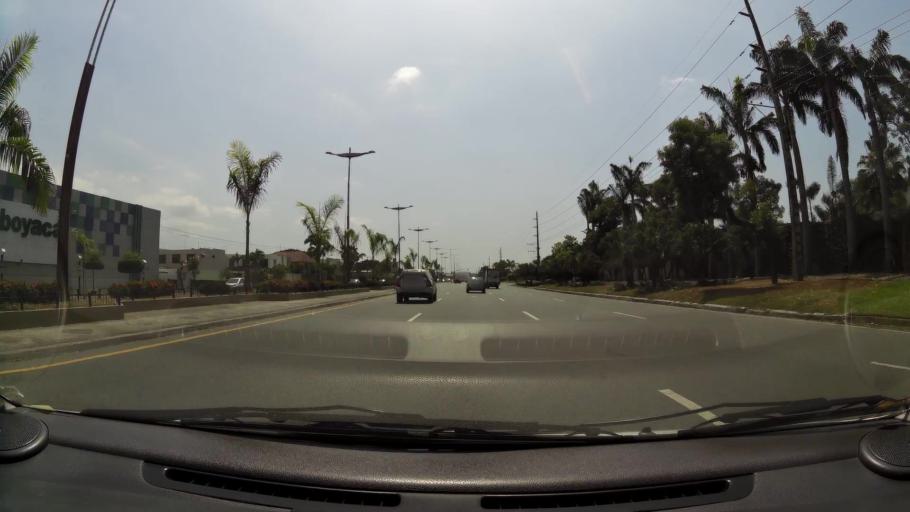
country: EC
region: Guayas
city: Eloy Alfaro
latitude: -2.1087
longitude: -79.8719
